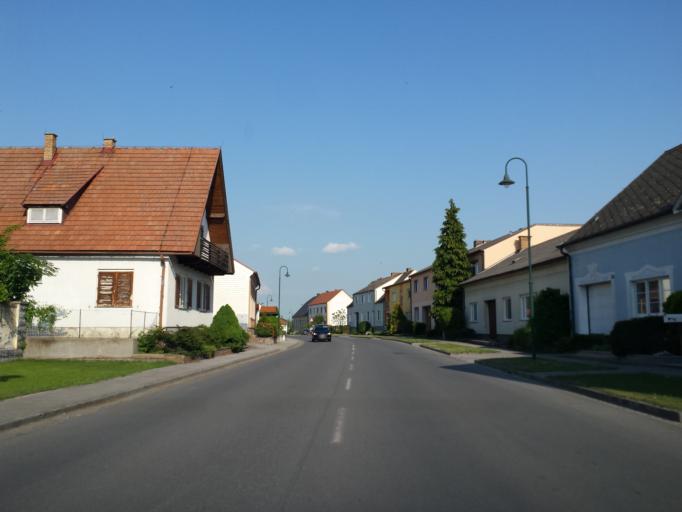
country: AT
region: Lower Austria
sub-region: Politischer Bezirk Ganserndorf
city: Angern an der March
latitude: 48.3413
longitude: 16.8369
